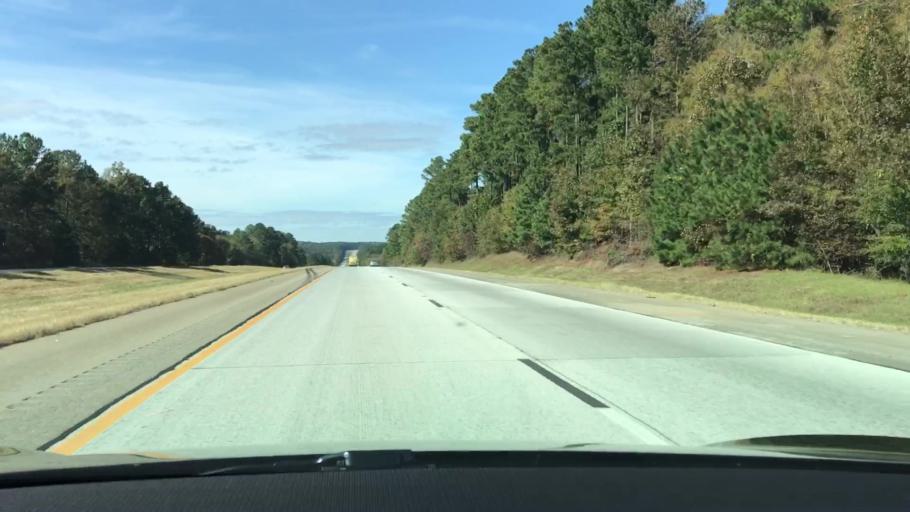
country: US
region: Georgia
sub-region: Greene County
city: Greensboro
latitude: 33.5355
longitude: -83.2537
